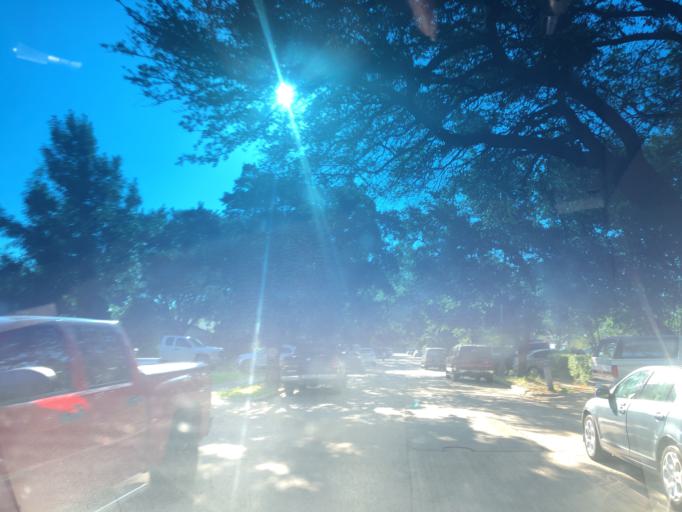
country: US
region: Texas
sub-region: Dallas County
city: Grand Prairie
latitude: 32.6983
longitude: -97.0004
